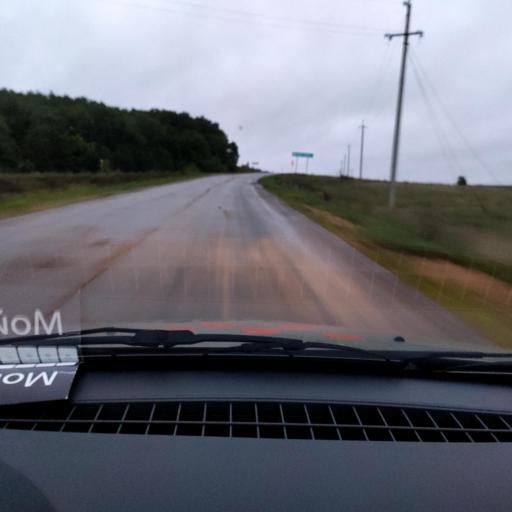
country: RU
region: Bashkortostan
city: Kudeyevskiy
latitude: 54.8818
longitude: 56.5863
